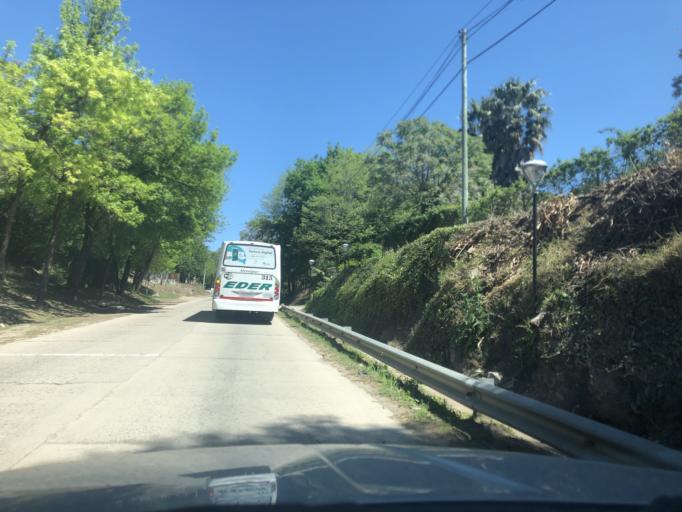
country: AR
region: Cordoba
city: La Granja
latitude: -31.0101
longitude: -64.2695
